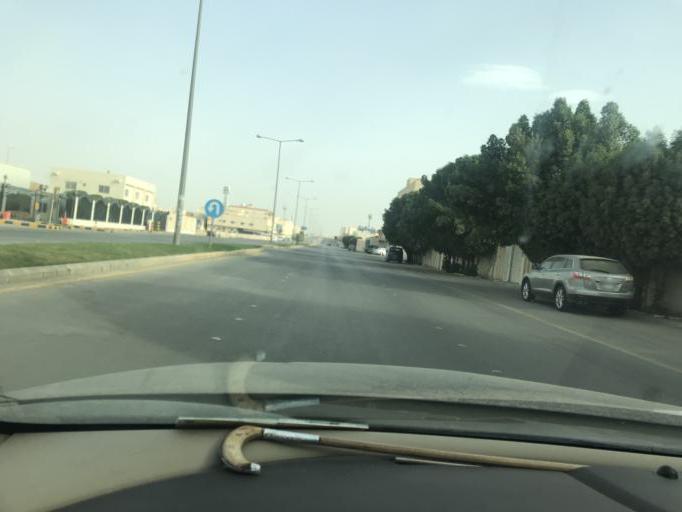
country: SA
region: Ar Riyad
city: Riyadh
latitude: 24.7868
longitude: 46.7130
